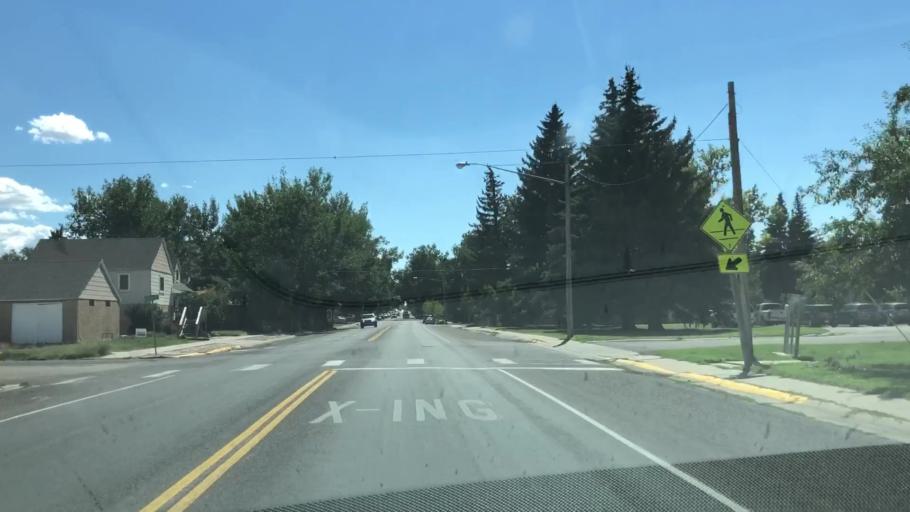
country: US
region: Wyoming
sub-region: Albany County
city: Laramie
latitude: 41.3211
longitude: -105.5846
